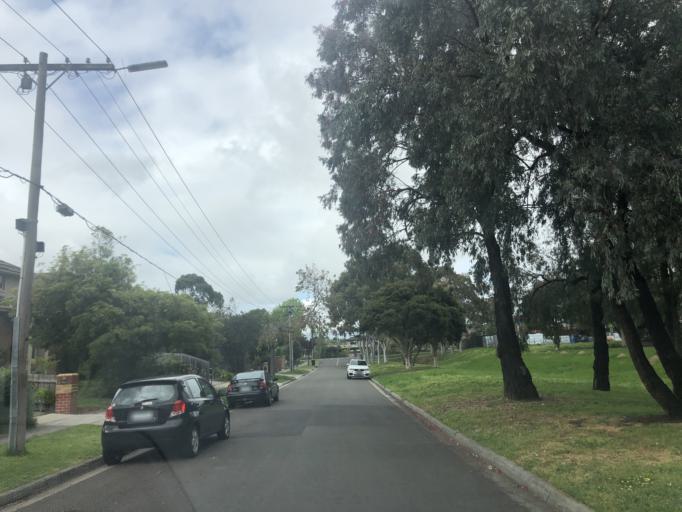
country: AU
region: Victoria
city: Burwood East
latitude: -37.8707
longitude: 145.1463
